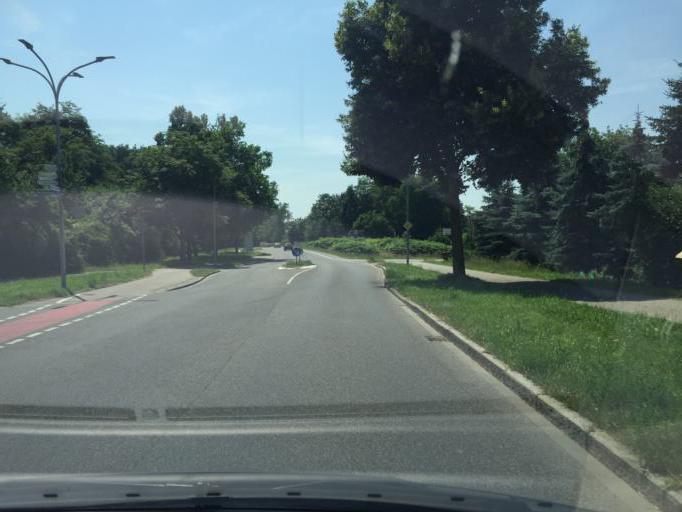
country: DE
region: Baden-Wuerttemberg
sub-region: Freiburg Region
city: Rielasingen-Worblingen
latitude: 47.7420
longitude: 8.8424
